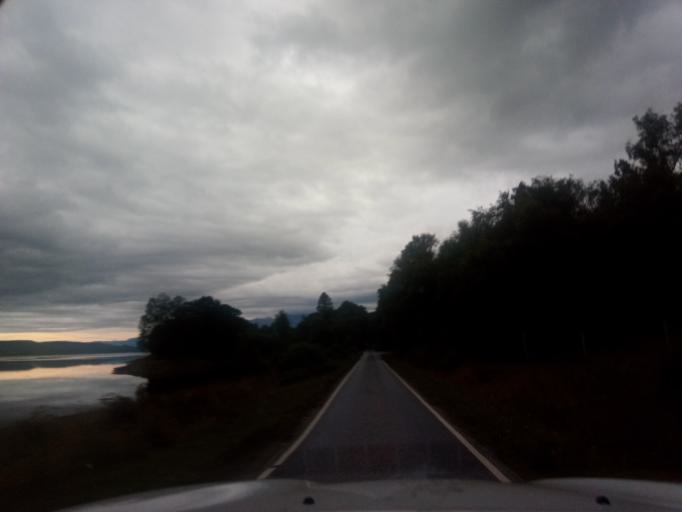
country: GB
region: Scotland
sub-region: Highland
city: Fort William
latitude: 56.8493
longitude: -5.3209
